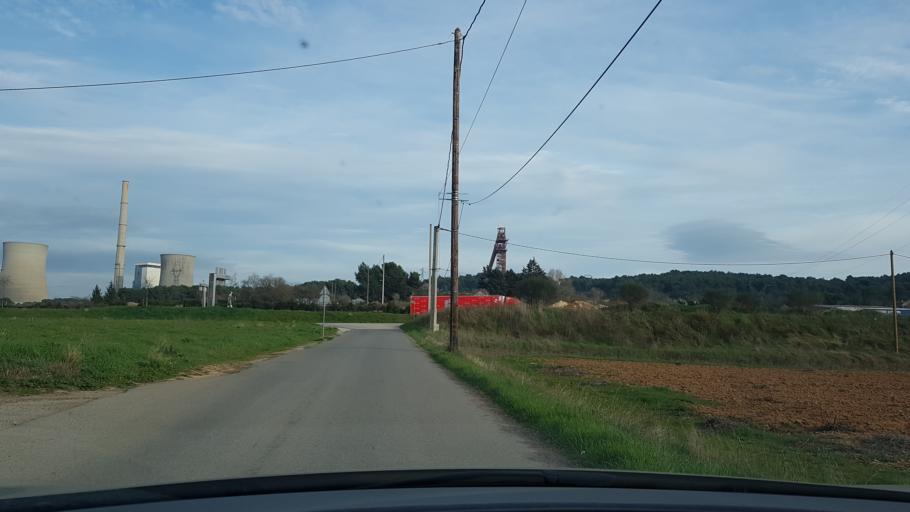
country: FR
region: Provence-Alpes-Cote d'Azur
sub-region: Departement des Bouches-du-Rhone
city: Gardanne
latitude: 43.4699
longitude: 5.4678
